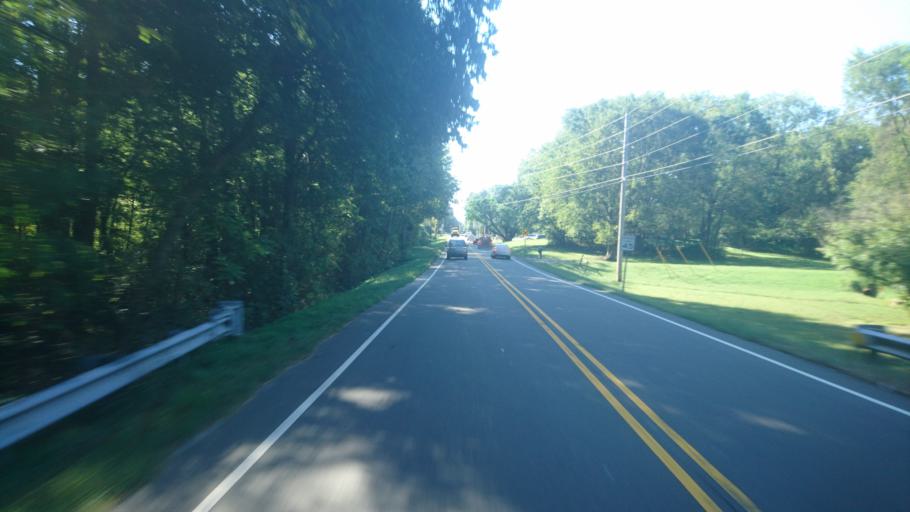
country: US
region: North Carolina
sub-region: Orange County
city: Chapel Hill
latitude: 35.9949
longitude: -79.0726
